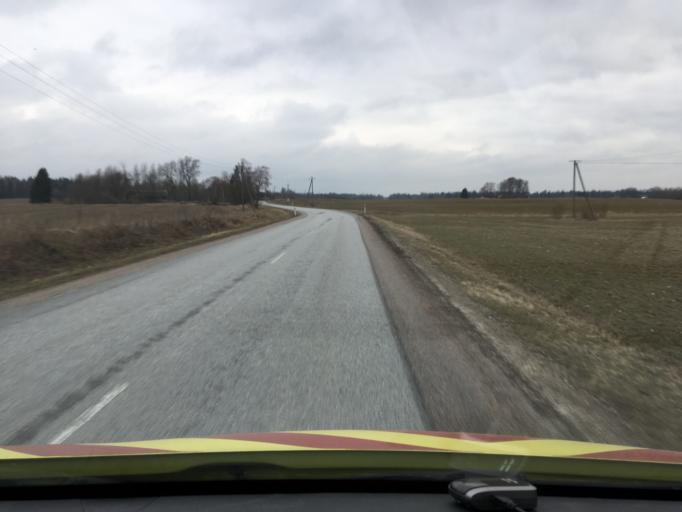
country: EE
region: Raplamaa
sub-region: Rapla vald
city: Rapla
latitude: 59.0274
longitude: 24.8382
